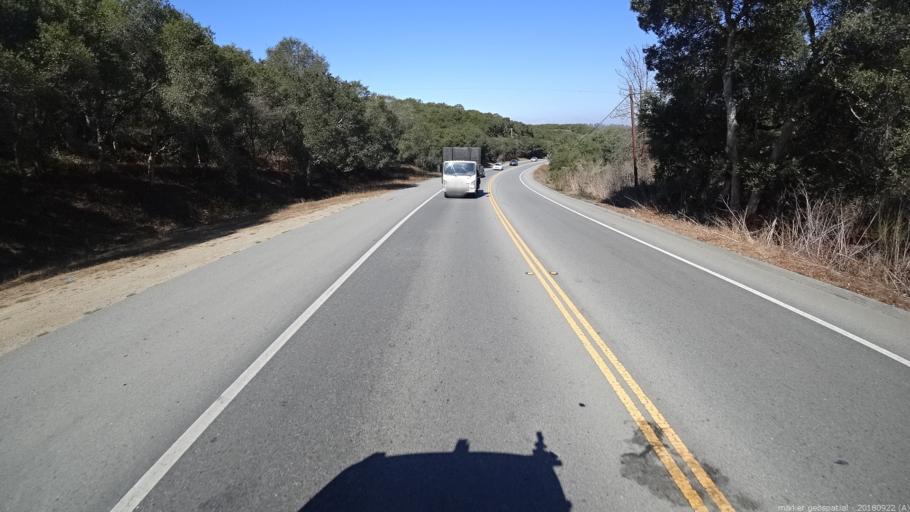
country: US
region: California
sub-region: Monterey County
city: Elkhorn
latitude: 36.8352
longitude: -121.6818
